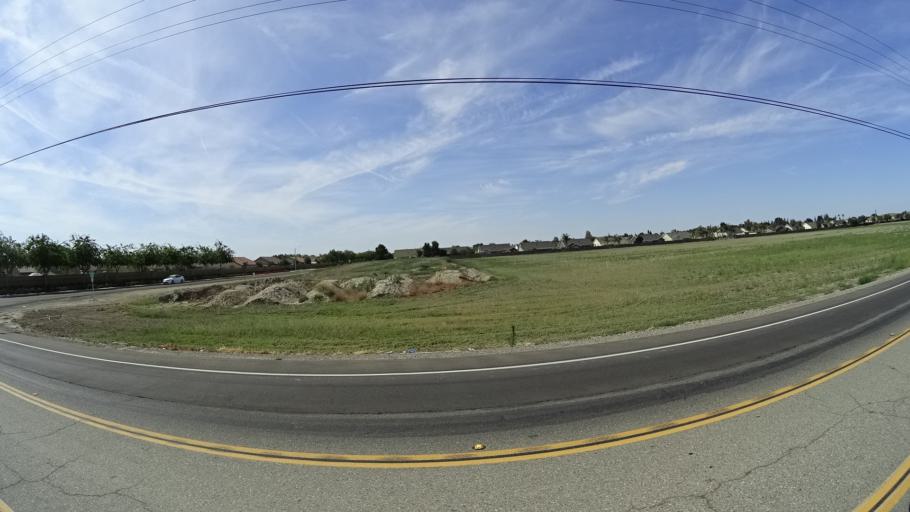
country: US
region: California
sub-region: Kings County
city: Lucerne
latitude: 36.3573
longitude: -119.6689
